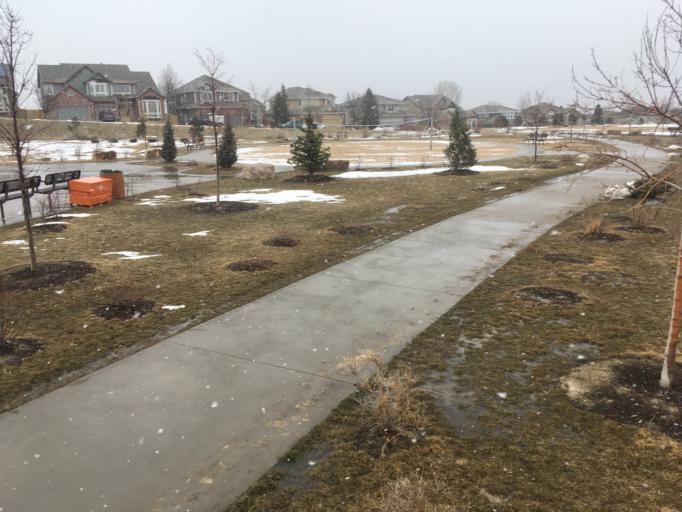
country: US
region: Colorado
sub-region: Boulder County
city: Superior
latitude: 39.9233
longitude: -105.1620
